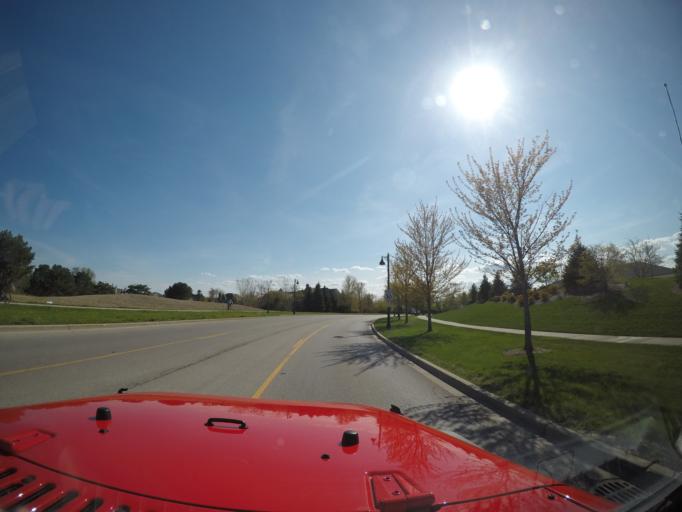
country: US
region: Illinois
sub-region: Cook County
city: Northbrook
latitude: 42.0879
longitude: -87.8329
